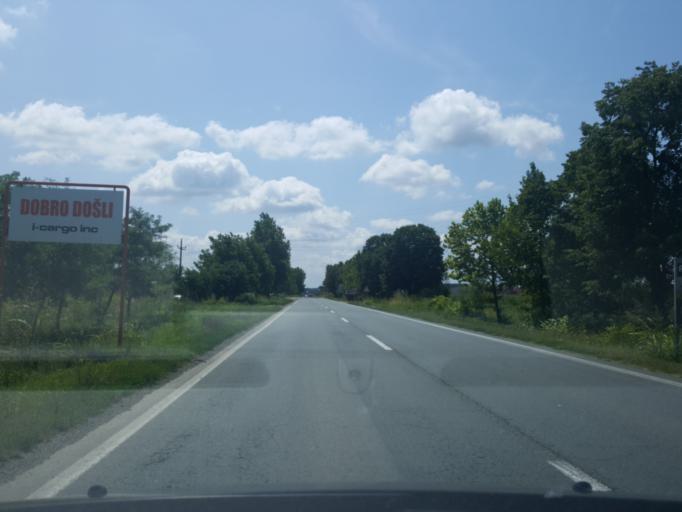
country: RS
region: Autonomna Pokrajina Vojvodina
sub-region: Sremski Okrug
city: Sremska Mitrovica
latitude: 44.9799
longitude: 19.6388
